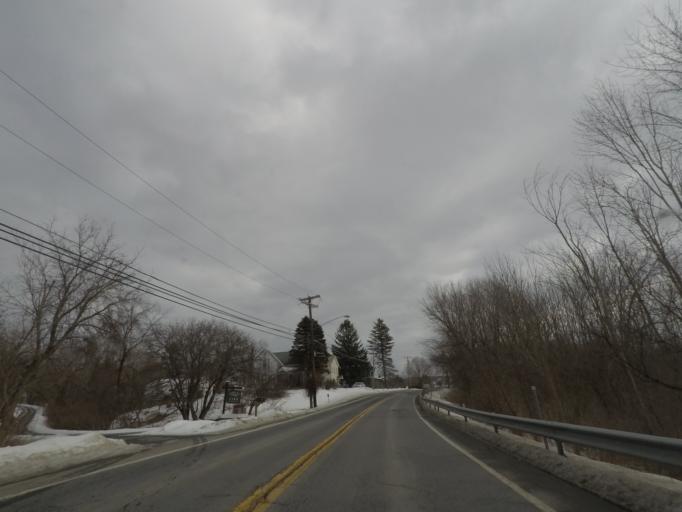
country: US
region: New York
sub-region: Washington County
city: Greenwich
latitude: 43.0845
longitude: -73.4890
